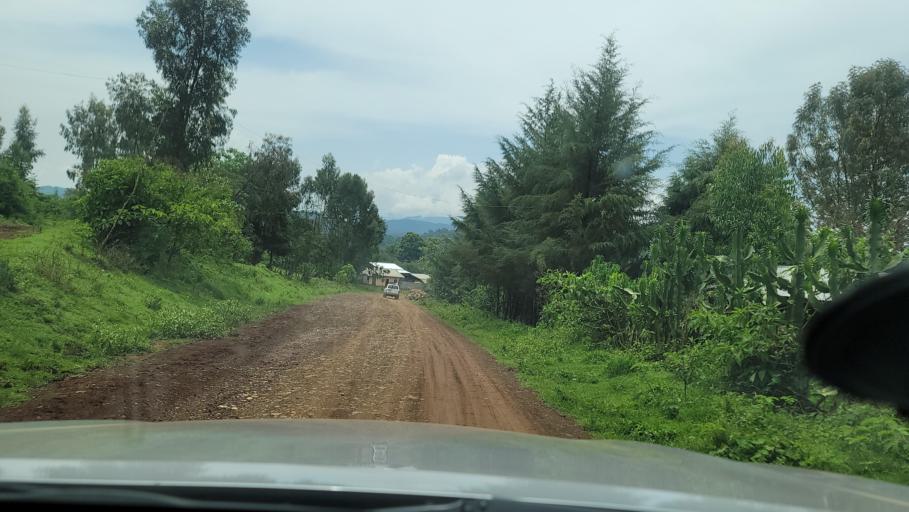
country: ET
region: Oromiya
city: Agaro
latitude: 7.7373
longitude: 36.2571
